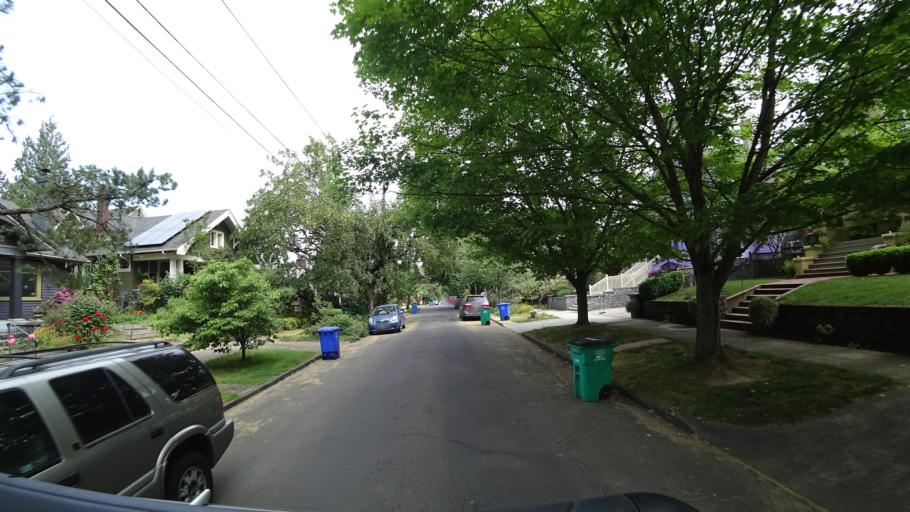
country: US
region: Oregon
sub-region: Multnomah County
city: Portland
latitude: 45.5360
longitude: -122.6129
